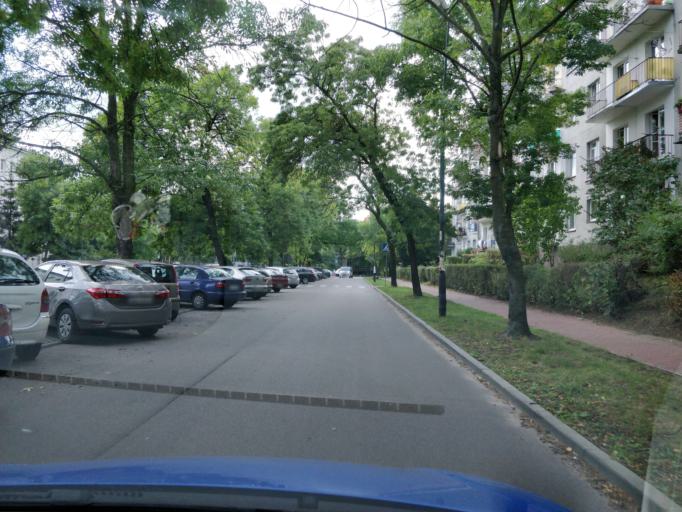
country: PL
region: Silesian Voivodeship
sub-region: Sosnowiec
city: Sosnowiec
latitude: 50.2713
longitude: 19.1329
